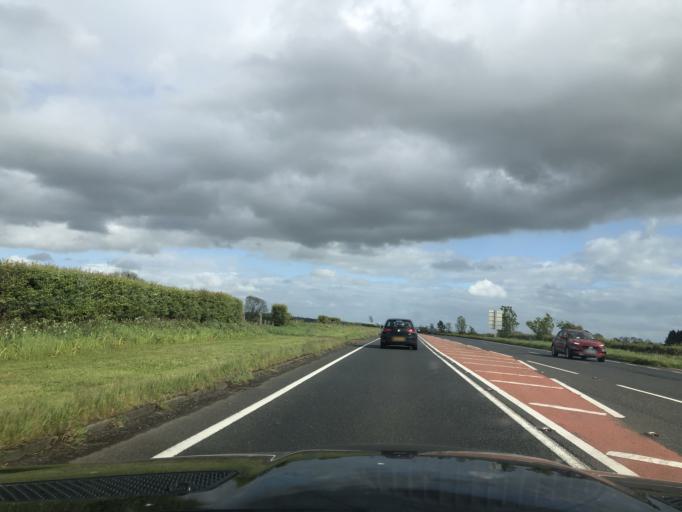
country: GB
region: Northern Ireland
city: Dunloy
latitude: 55.0304
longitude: -6.3970
